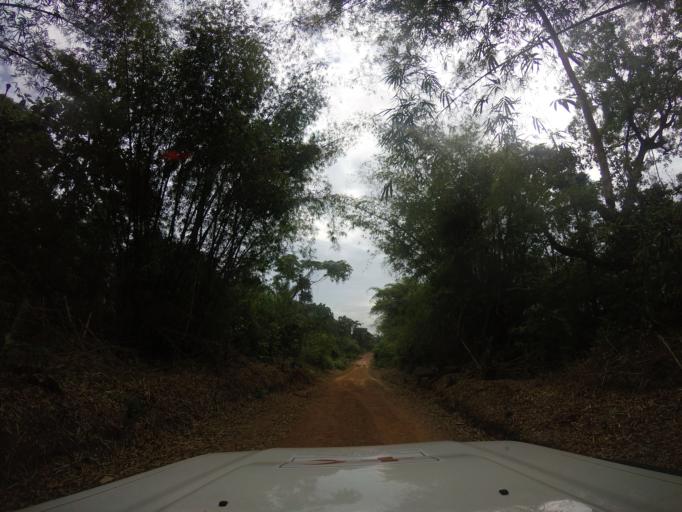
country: SL
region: Southern Province
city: Zimmi
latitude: 7.1499
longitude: -11.2661
